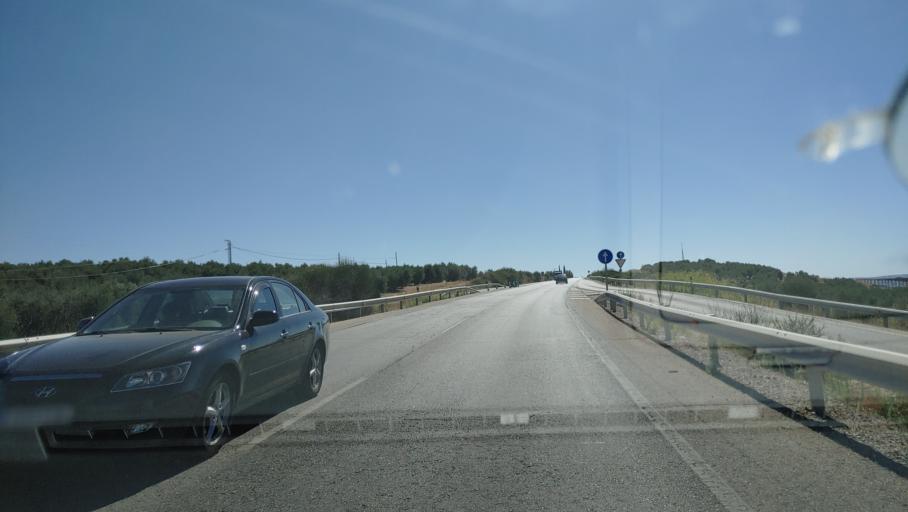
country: ES
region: Andalusia
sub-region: Provincia de Jaen
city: Villacarrillo
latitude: 38.1286
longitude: -3.0588
